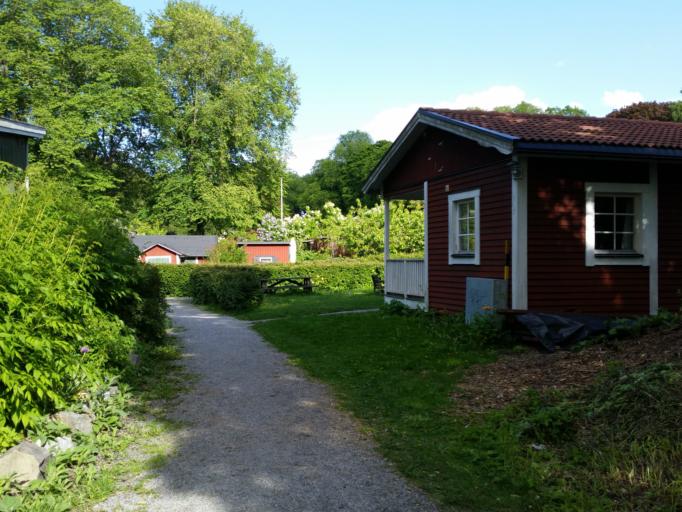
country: SE
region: Stockholm
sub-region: Stockholms Kommun
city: Arsta
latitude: 59.3149
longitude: 18.0455
